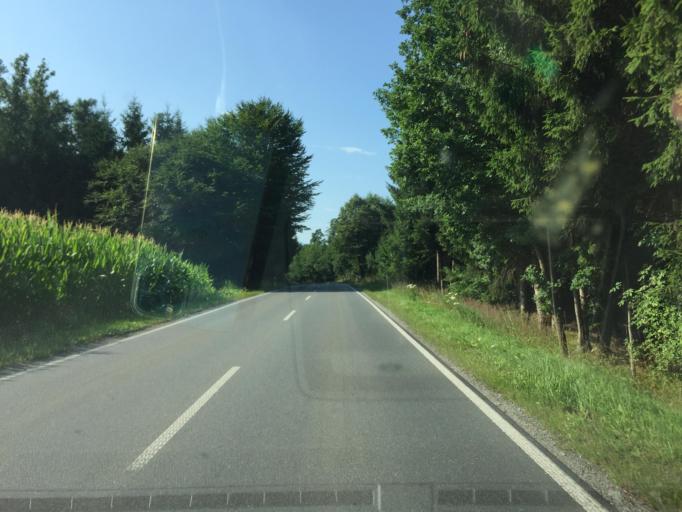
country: DE
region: Bavaria
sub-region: Upper Bavaria
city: Tuntenhausen
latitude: 47.9135
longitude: 11.9880
